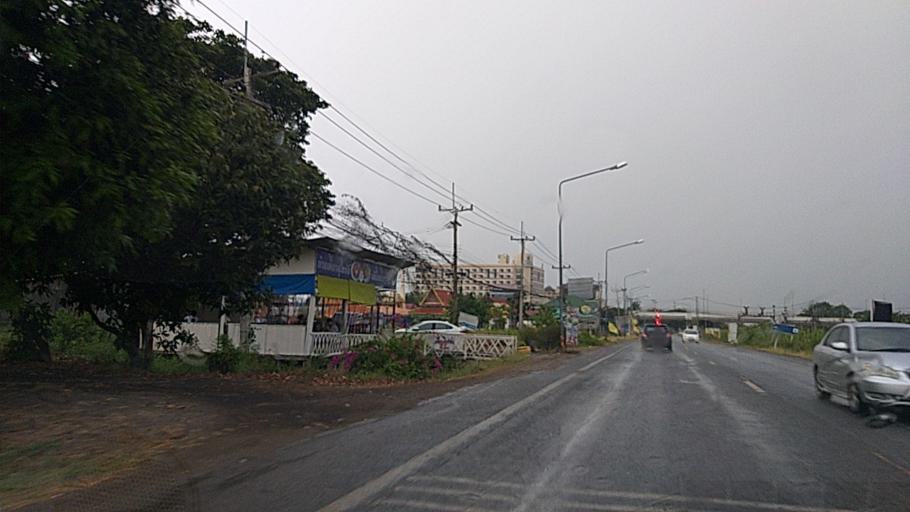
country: TH
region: Phra Nakhon Si Ayutthaya
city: Phra Nakhon Si Ayutthaya
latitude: 14.3497
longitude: 100.5840
